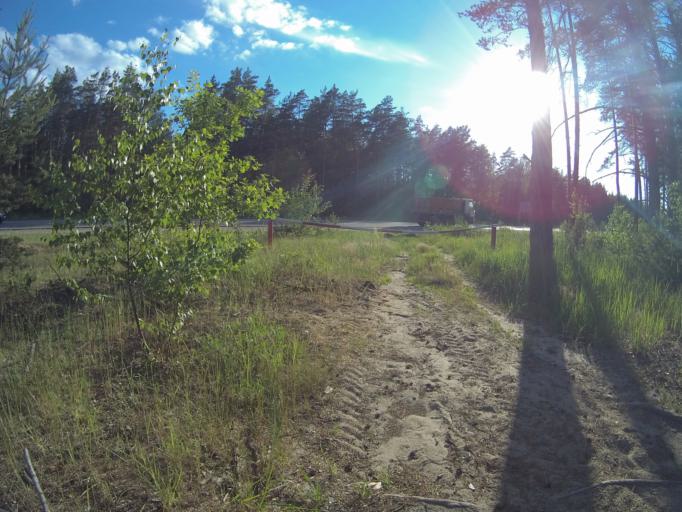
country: RU
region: Vladimir
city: Kommunar
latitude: 56.0857
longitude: 40.4618
